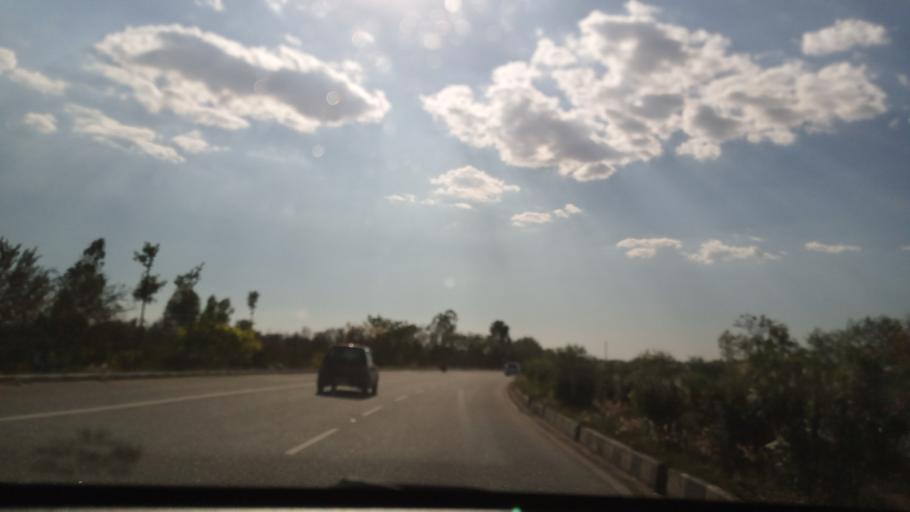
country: IN
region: Karnataka
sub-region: Kolar
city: Kolar
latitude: 13.1273
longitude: 77.9988
